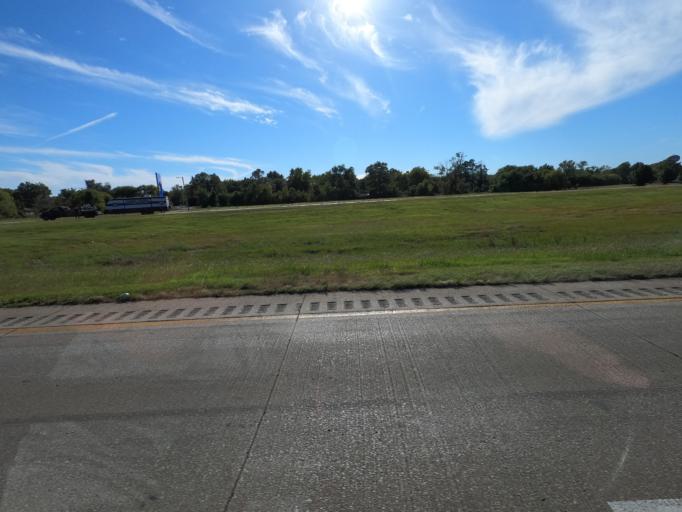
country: US
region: Arkansas
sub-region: Crittenden County
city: West Memphis
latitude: 35.1541
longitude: -90.1455
